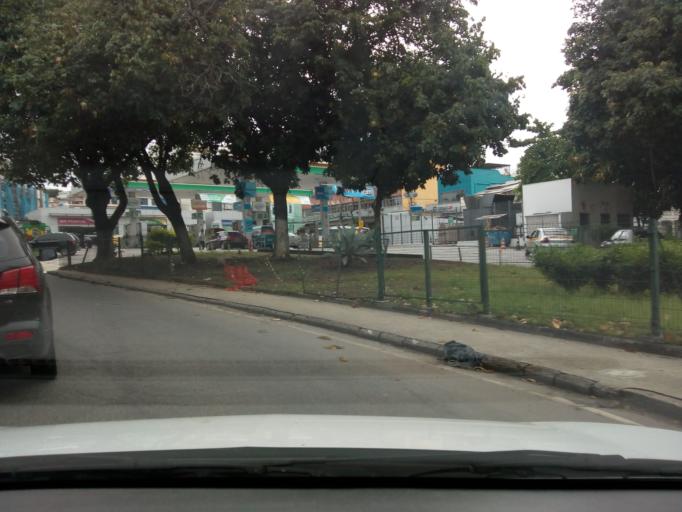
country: BR
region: Rio de Janeiro
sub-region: Rio De Janeiro
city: Rio de Janeiro
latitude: -22.8985
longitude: -43.2230
